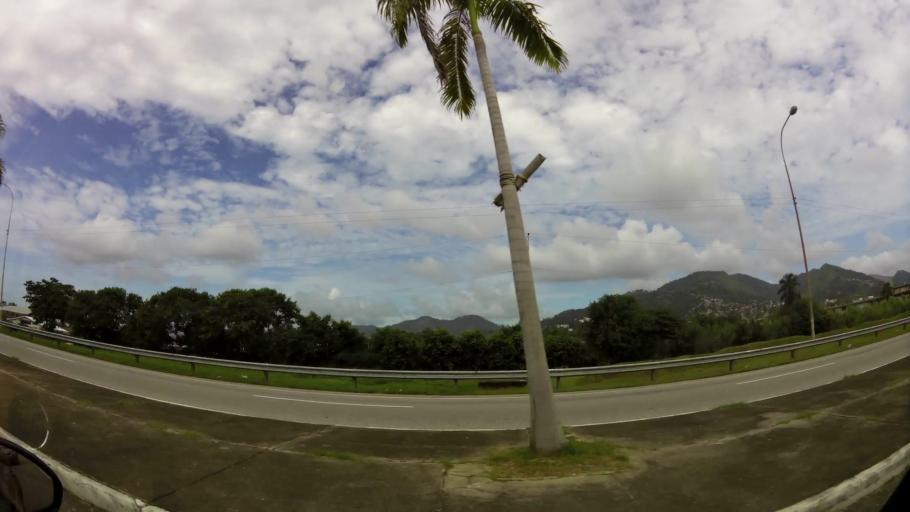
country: TT
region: City of Port of Spain
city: Mucurapo
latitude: 10.6631
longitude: -61.5331
